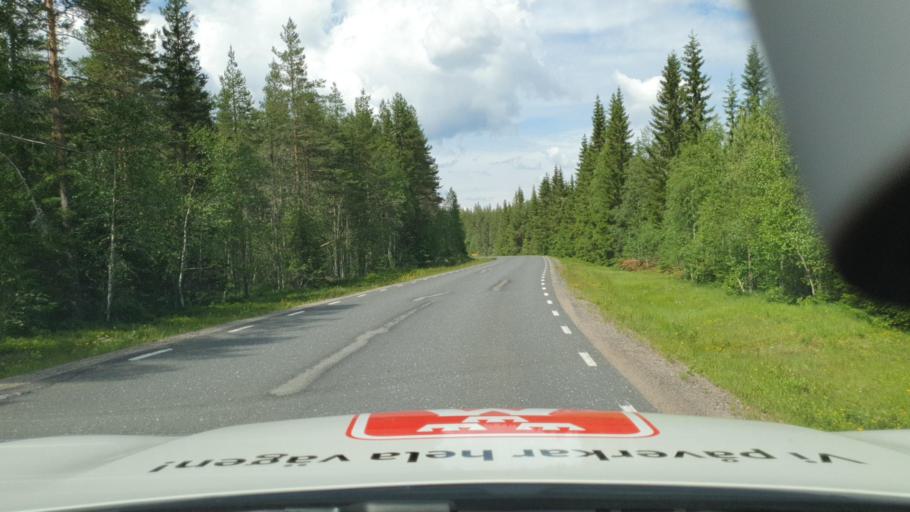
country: SE
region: Vaermland
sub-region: Torsby Kommun
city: Torsby
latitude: 60.6116
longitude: 12.7204
